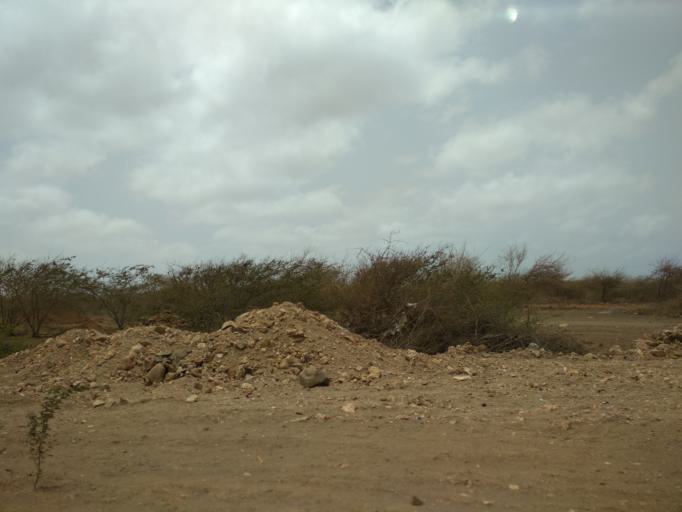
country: CV
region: Sal
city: Espargos
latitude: 16.7572
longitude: -22.9754
